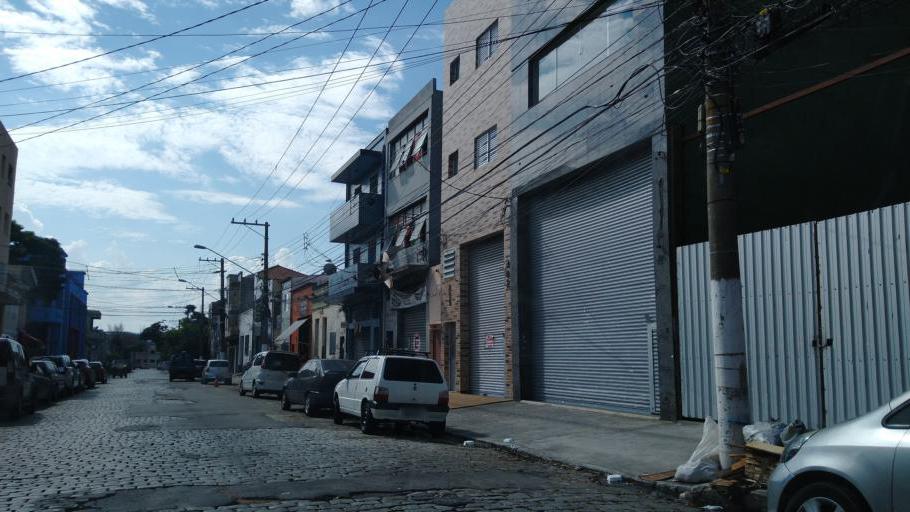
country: BR
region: Sao Paulo
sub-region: Sao Paulo
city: Sao Paulo
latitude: -23.5368
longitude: -46.6031
